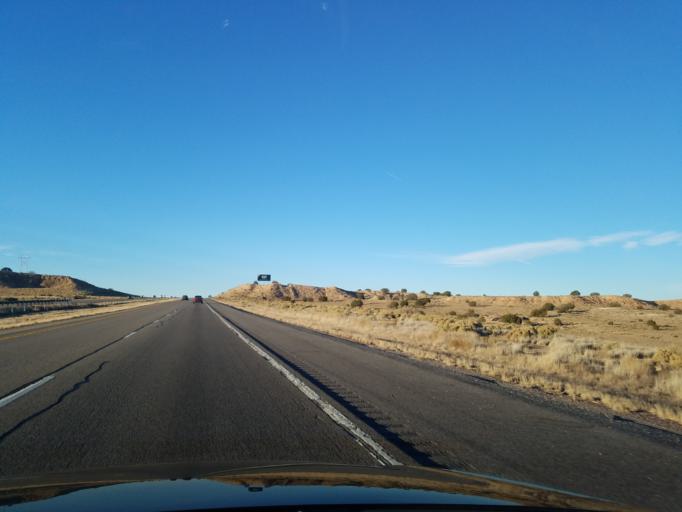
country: US
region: New Mexico
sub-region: Sandoval County
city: San Felipe Pueblo
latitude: 35.4344
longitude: -106.3791
